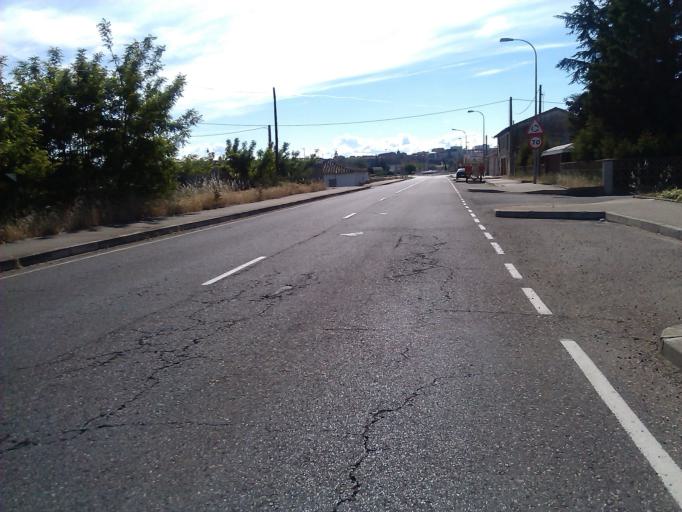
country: ES
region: Castille and Leon
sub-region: Provincia de Leon
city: San Justo de la Vega
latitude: 42.4544
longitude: -6.0366
